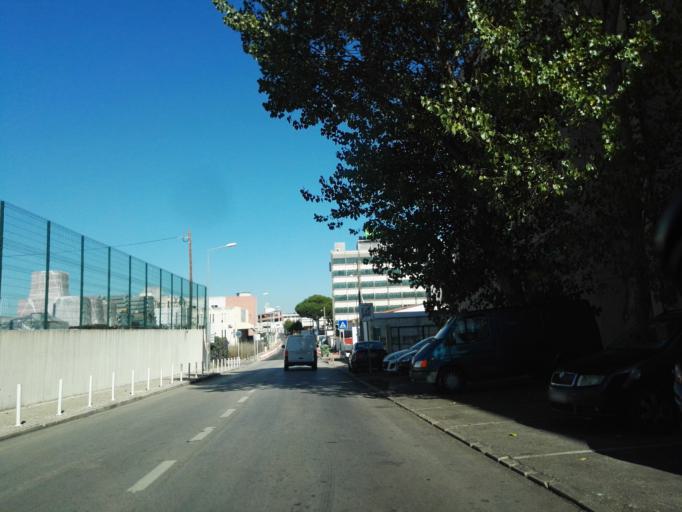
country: PT
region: Lisbon
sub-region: Loures
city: Sacavem
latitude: 38.7850
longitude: -9.1214
